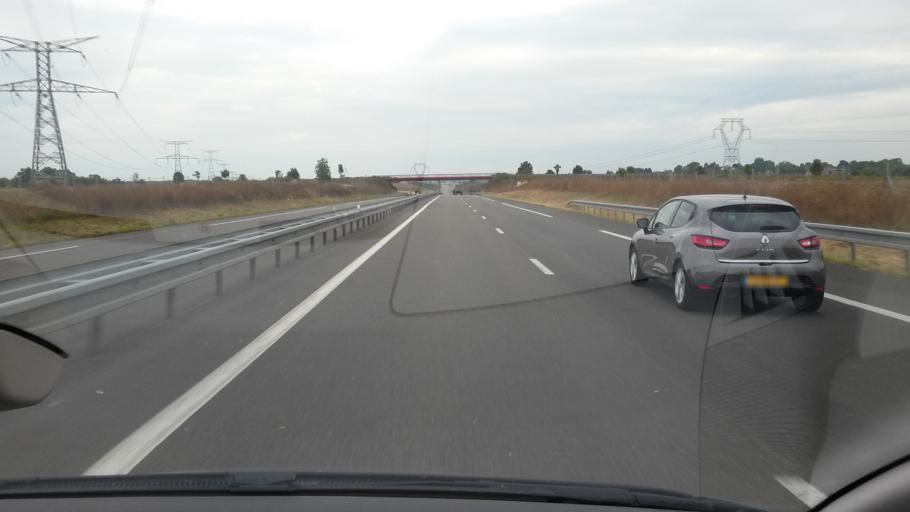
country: FR
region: Champagne-Ardenne
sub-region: Departement des Ardennes
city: Rethel
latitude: 49.5641
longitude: 4.4680
